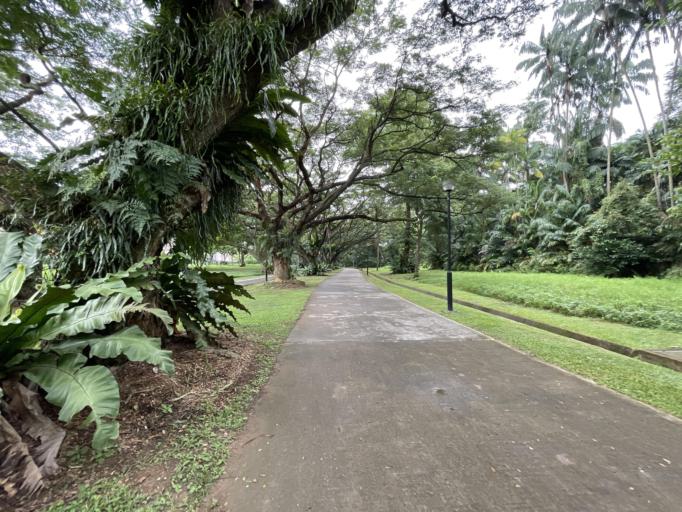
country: SG
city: Singapore
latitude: 1.2874
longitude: 103.7737
